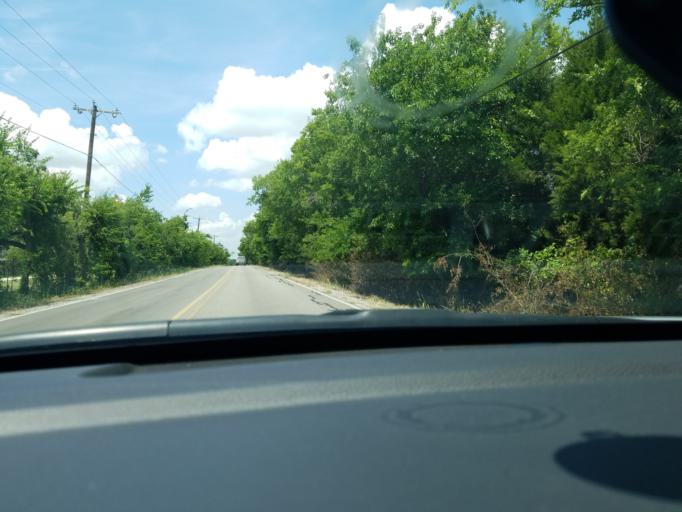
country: US
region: Texas
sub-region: Dallas County
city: Sunnyvale
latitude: 32.8140
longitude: -96.5709
